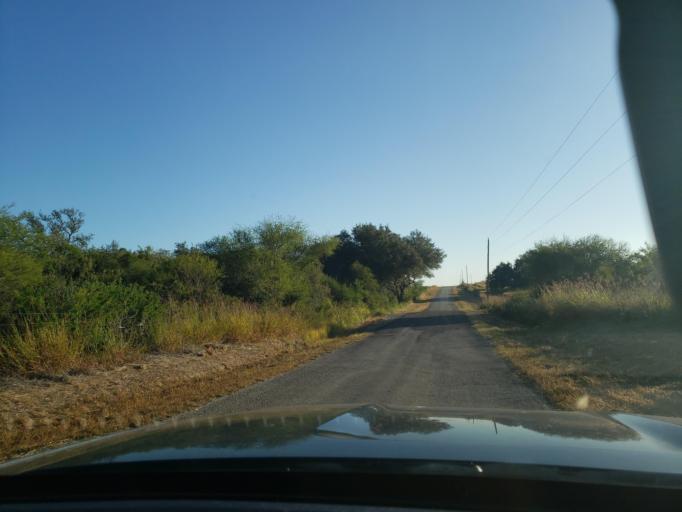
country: US
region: Texas
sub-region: Bee County
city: Beeville
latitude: 28.4247
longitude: -97.7033
